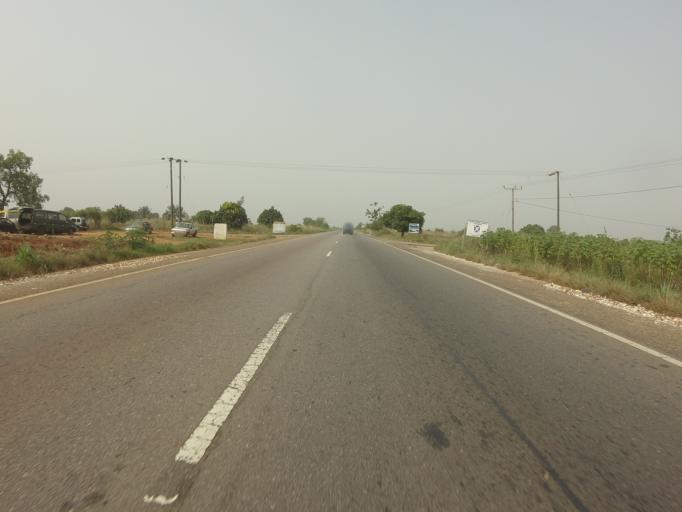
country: GH
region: Volta
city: Anloga
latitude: 5.9140
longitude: 0.5227
